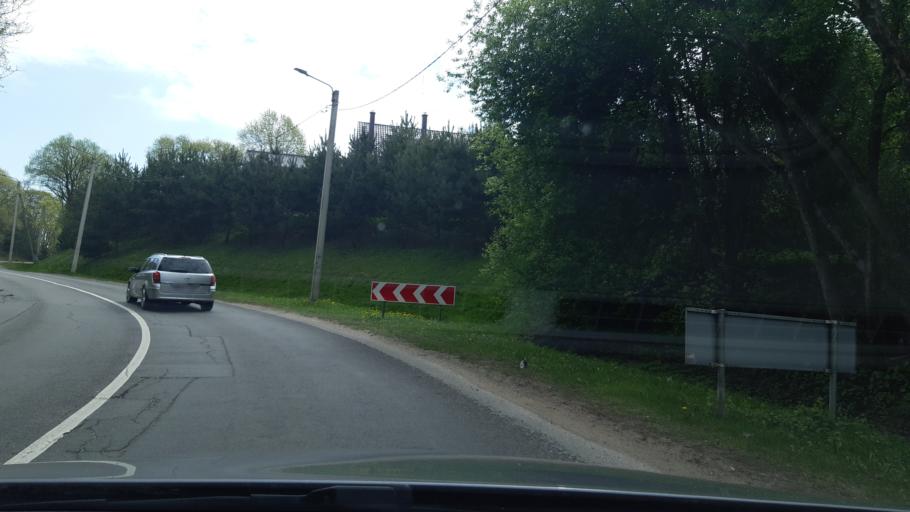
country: LT
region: Kauno apskritis
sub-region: Kaunas
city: Silainiai
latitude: 54.9236
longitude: 23.8657
